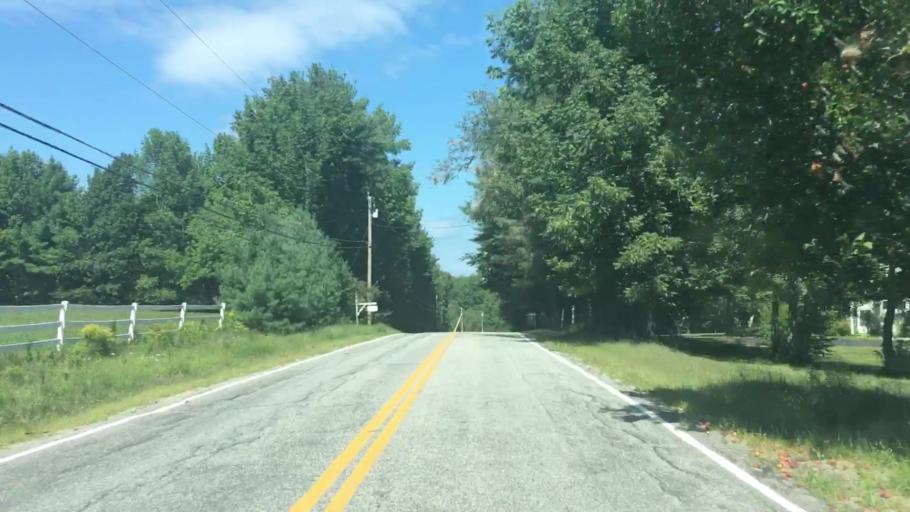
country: US
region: Maine
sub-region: Kennebec County
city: Monmouth
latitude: 44.1712
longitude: -69.9421
